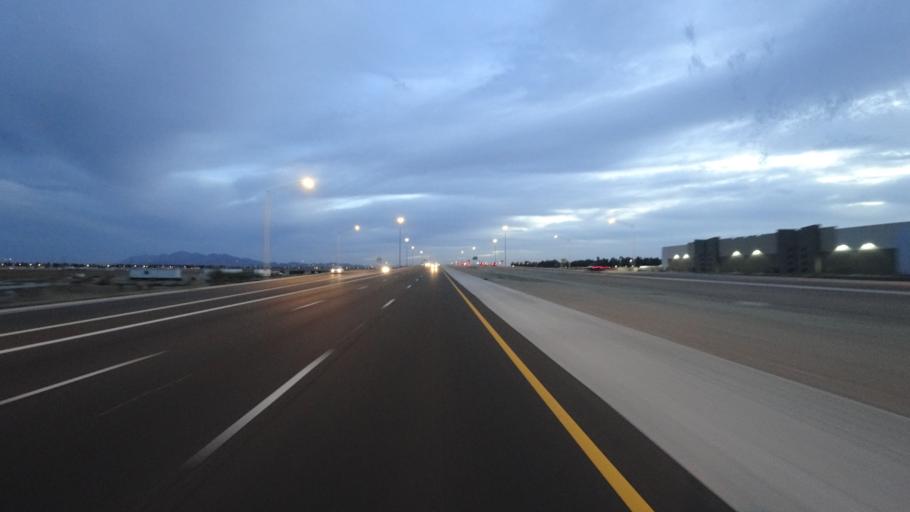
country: US
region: Arizona
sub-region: Maricopa County
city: Citrus Park
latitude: 33.4975
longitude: -112.4195
